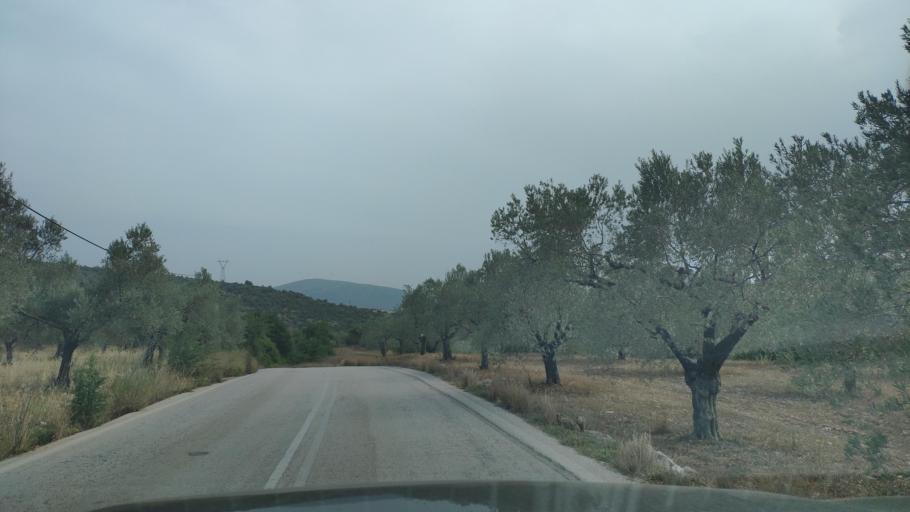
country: GR
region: Peloponnese
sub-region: Nomos Argolidos
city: Palaia Epidavros
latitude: 37.5757
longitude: 23.1502
